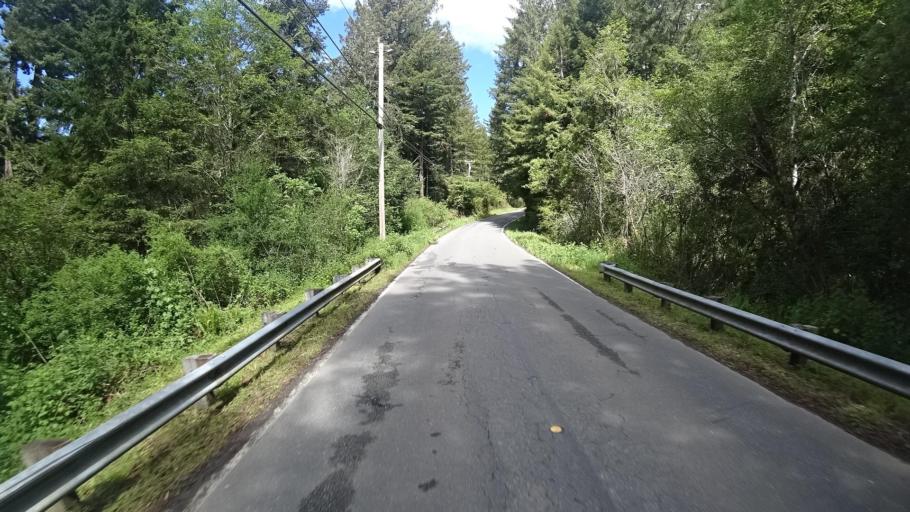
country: US
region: California
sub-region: Humboldt County
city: Blue Lake
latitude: 40.9399
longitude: -124.0237
